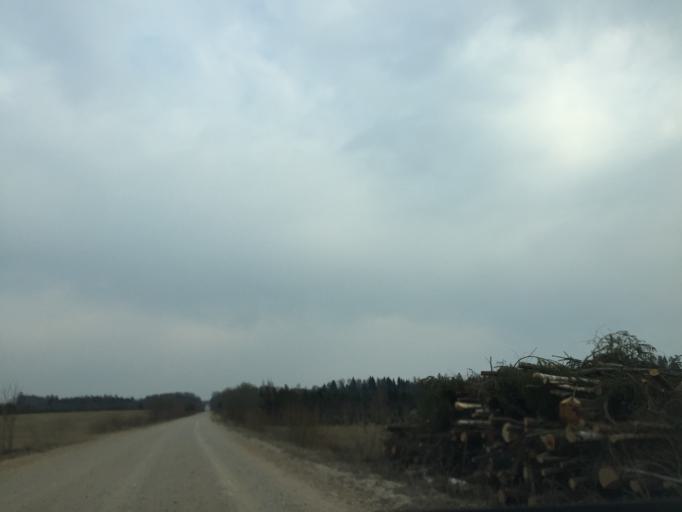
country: LV
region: Priekuli
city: Priekuli
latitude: 57.1883
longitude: 25.4558
